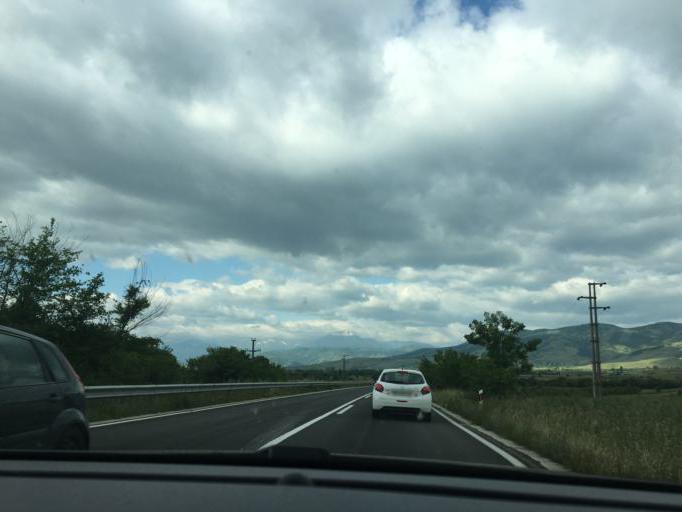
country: MK
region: Mogila
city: Dolno Srpci
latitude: 41.1801
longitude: 21.3991
